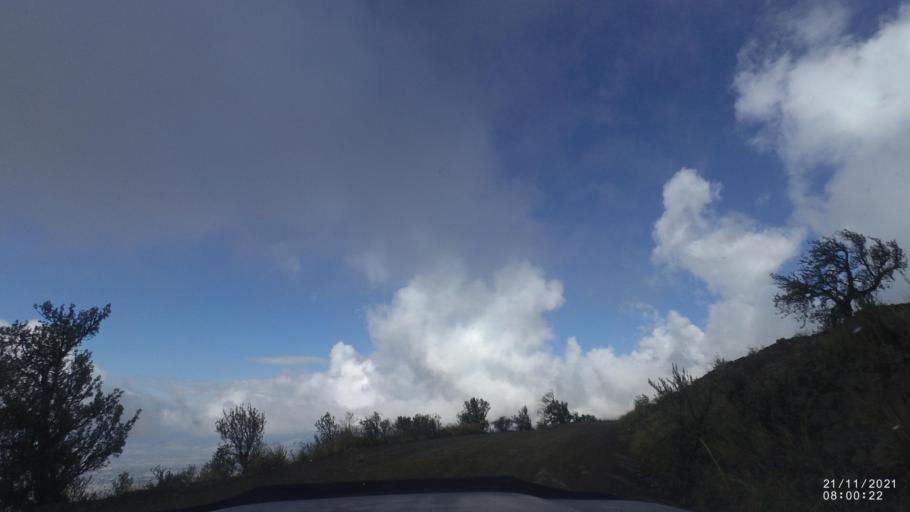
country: BO
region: Cochabamba
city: Cochabamba
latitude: -17.2918
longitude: -66.2180
